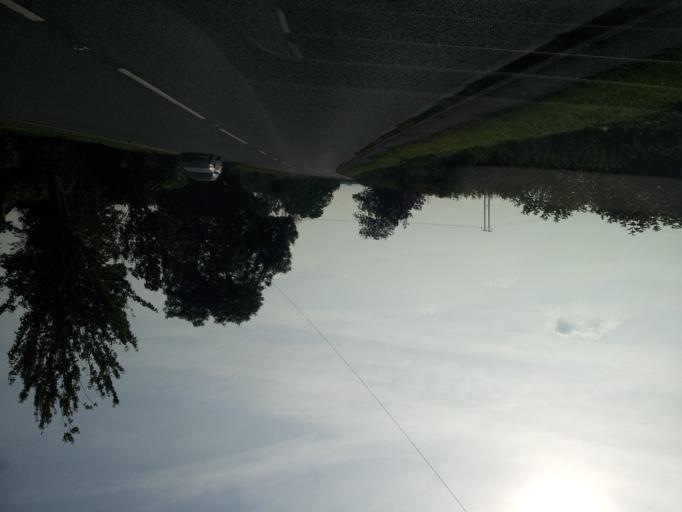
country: GB
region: England
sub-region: Lincolnshire
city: Long Bennington
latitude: 53.0370
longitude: -0.7703
